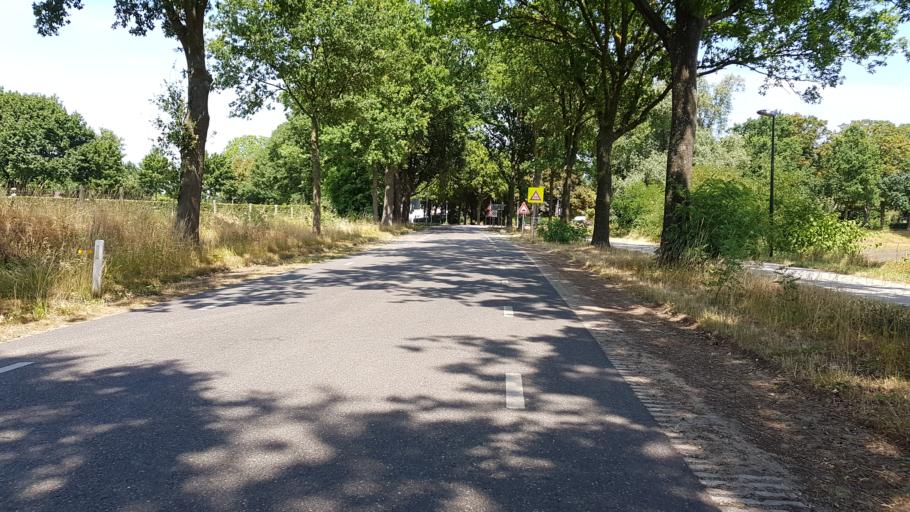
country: NL
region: Limburg
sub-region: Gemeente Maasgouw
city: Maasbracht
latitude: 51.0983
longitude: 5.8641
